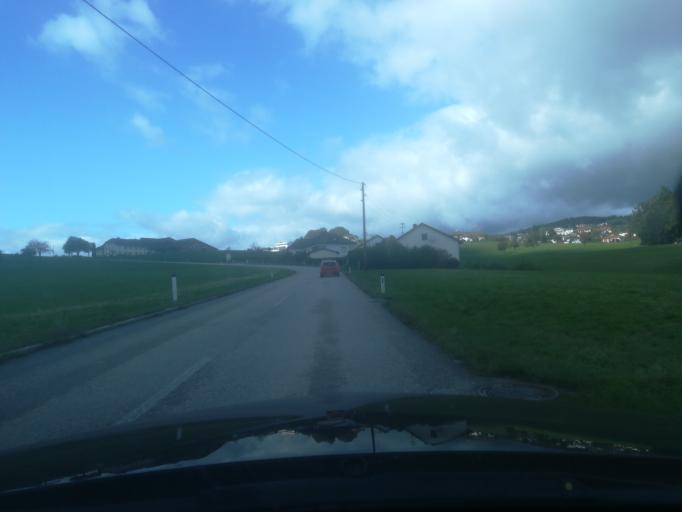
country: AT
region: Upper Austria
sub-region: Linz Stadt
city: Linz
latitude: 48.3515
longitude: 14.2637
